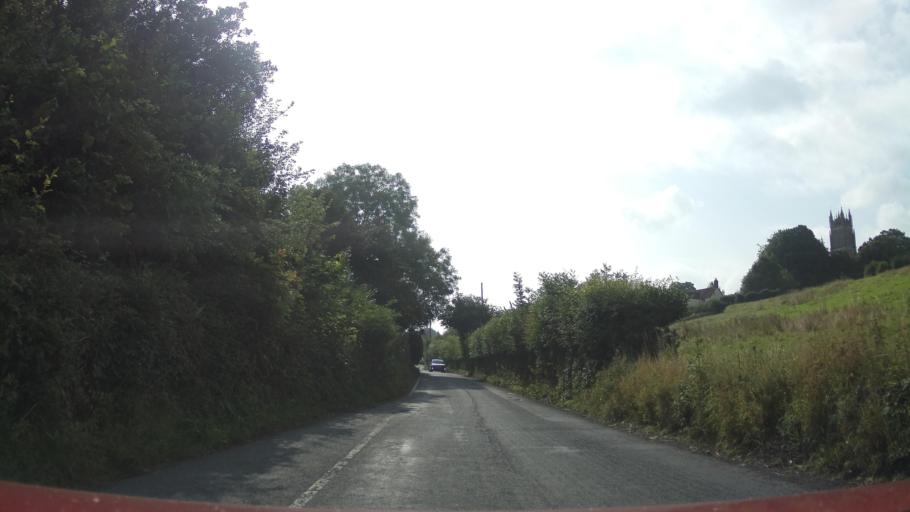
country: GB
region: England
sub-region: Bath and North East Somerset
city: Cameley
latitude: 51.2784
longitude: -2.5821
